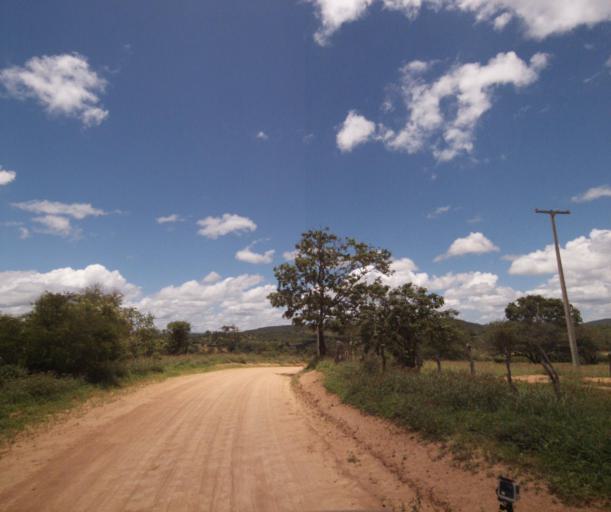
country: BR
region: Bahia
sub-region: Pocoes
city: Pocoes
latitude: -14.3820
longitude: -40.3666
